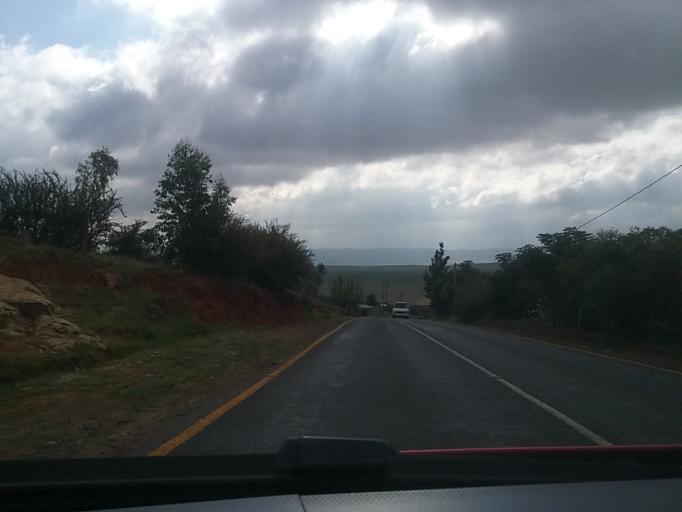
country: LS
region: Berea
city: Teyateyaneng
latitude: -29.1631
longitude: 27.7744
